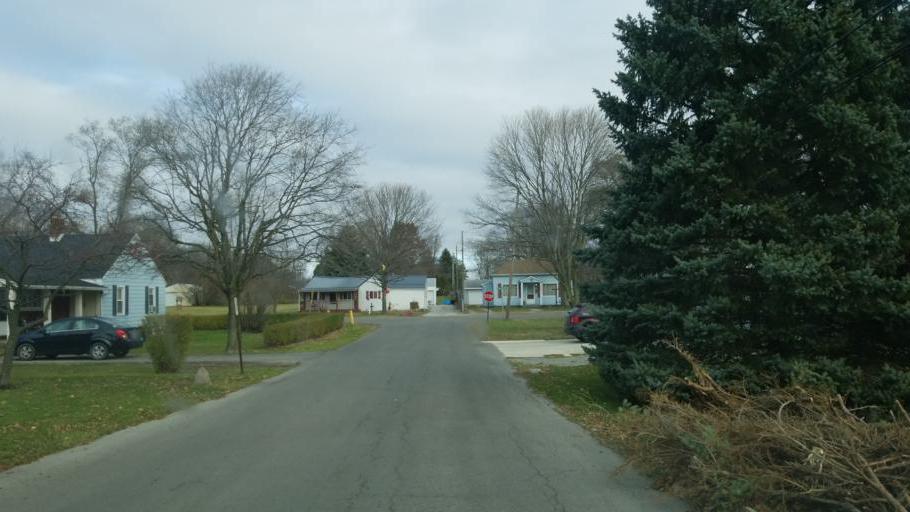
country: US
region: Ohio
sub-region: Hardin County
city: Kenton
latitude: 40.6537
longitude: -83.6214
